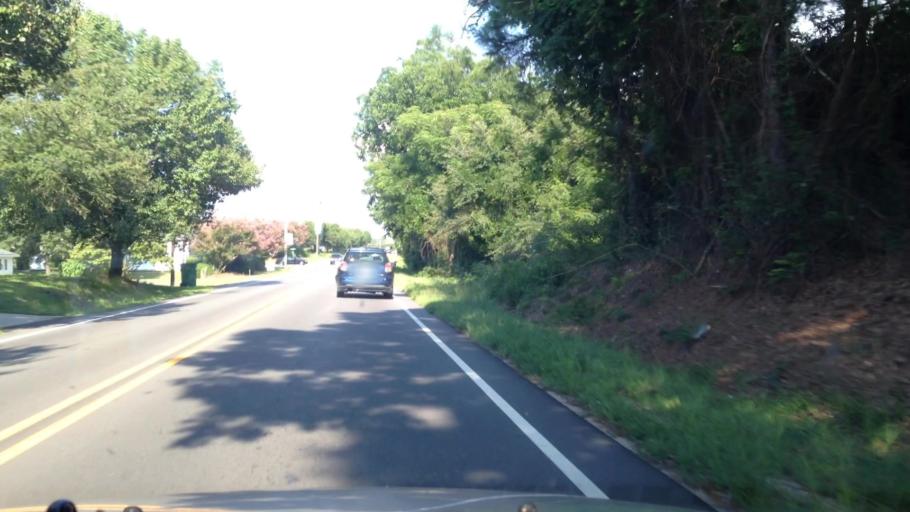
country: US
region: North Carolina
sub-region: Harnett County
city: Coats
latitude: 35.4123
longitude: -78.6790
